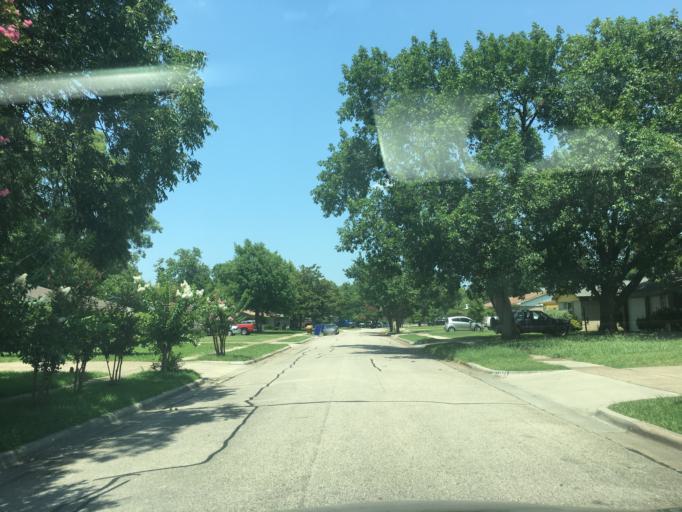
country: US
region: Texas
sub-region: Dallas County
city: Farmers Branch
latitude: 32.9333
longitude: -96.8794
